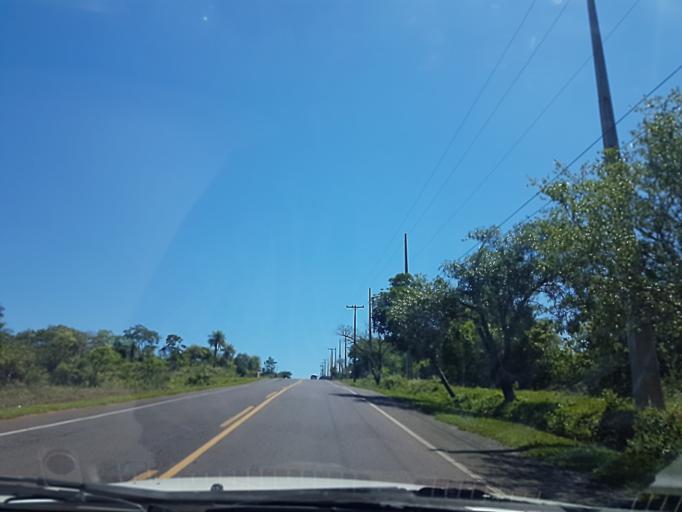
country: PY
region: Cordillera
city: Altos
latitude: -25.2528
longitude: -57.2409
